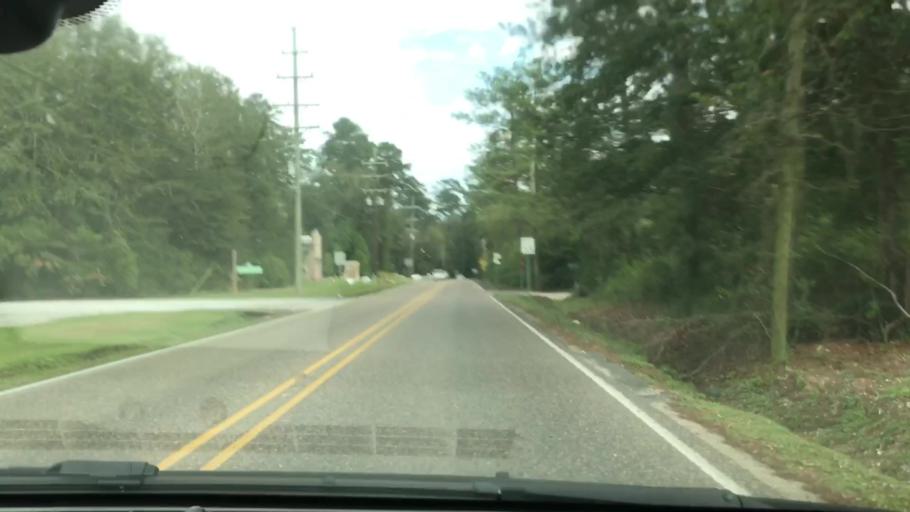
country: US
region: Louisiana
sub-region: Saint Tammany Parish
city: Abita Springs
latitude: 30.4827
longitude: -90.0432
